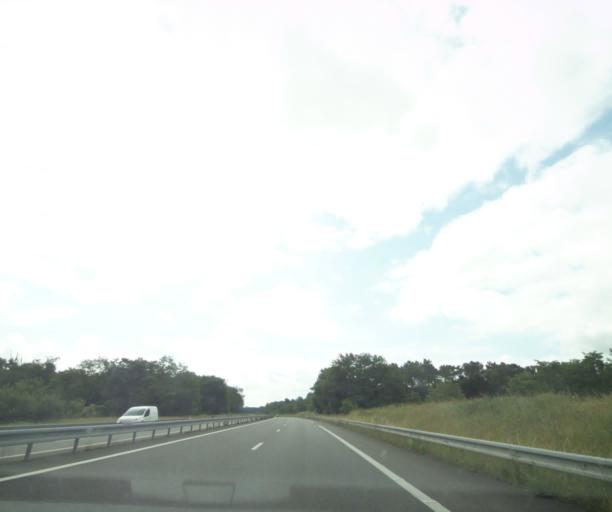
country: FR
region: Pays de la Loire
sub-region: Departement de Maine-et-Loire
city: Brion
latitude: 47.4354
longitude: -0.1691
